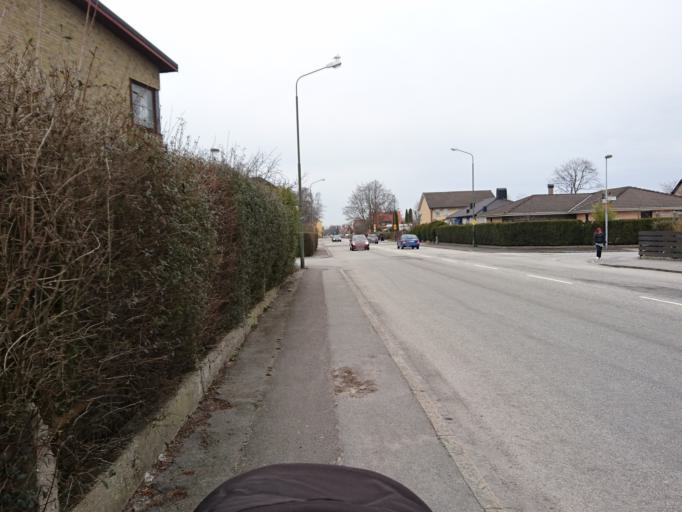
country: SE
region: Skane
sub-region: Malmo
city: Malmoe
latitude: 55.5752
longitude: 13.0345
